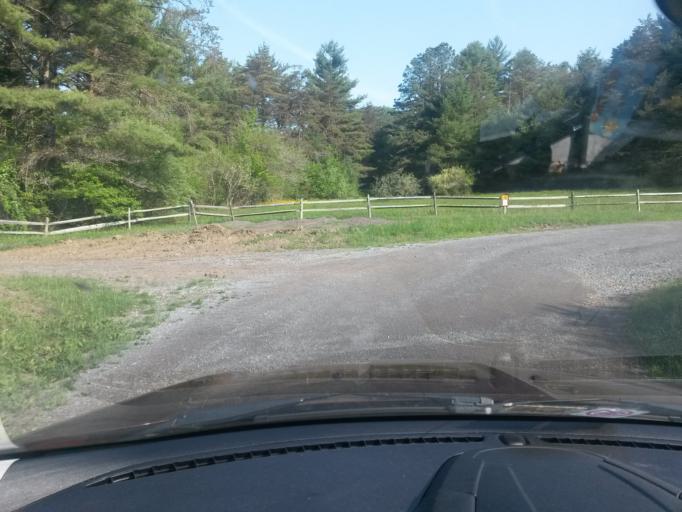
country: US
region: West Virginia
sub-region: Pocahontas County
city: Marlinton
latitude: 38.0349
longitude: -80.0347
